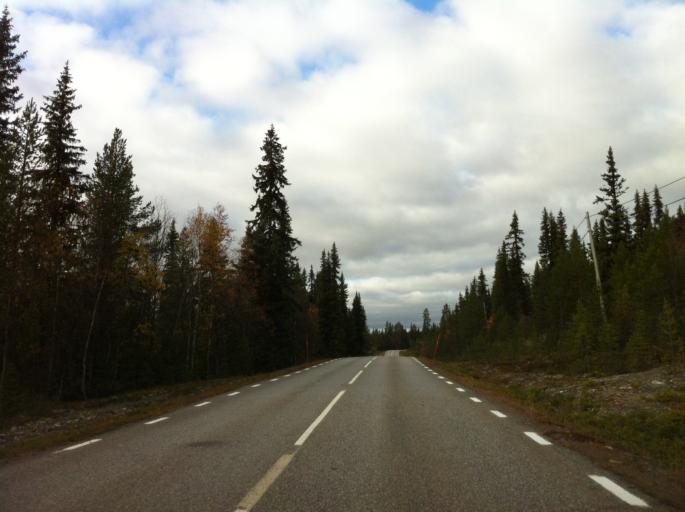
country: NO
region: Hedmark
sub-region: Engerdal
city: Engerdal
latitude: 61.9932
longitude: 12.4584
